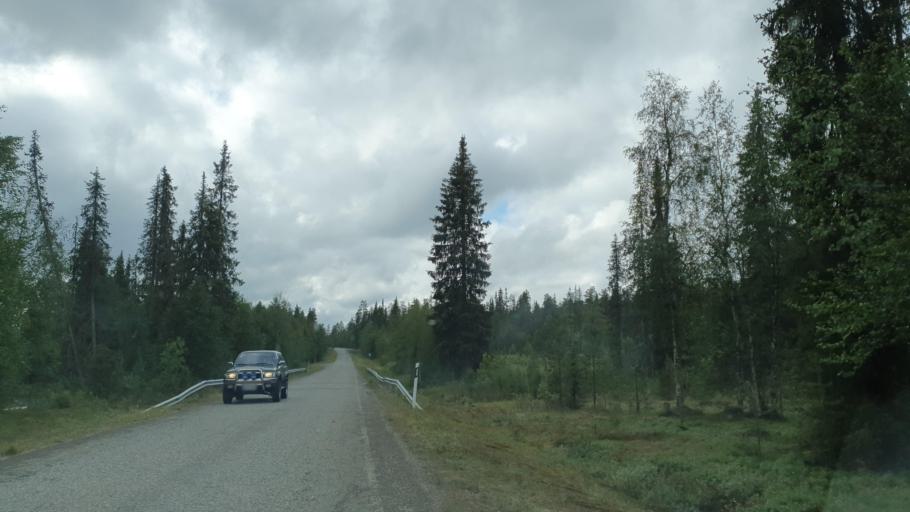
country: FI
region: Lapland
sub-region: Tunturi-Lappi
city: Muonio
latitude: 67.7182
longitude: 24.2221
